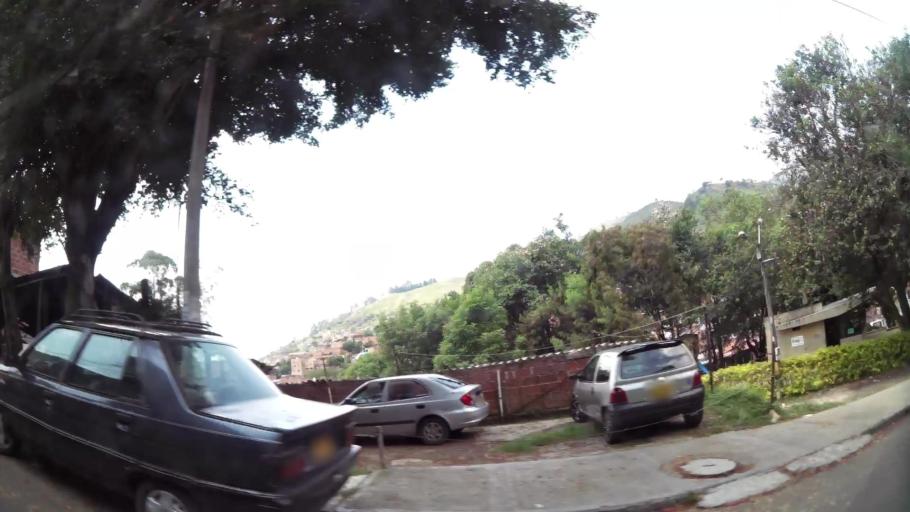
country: CO
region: Antioquia
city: Itagui
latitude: 6.1809
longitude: -75.6112
